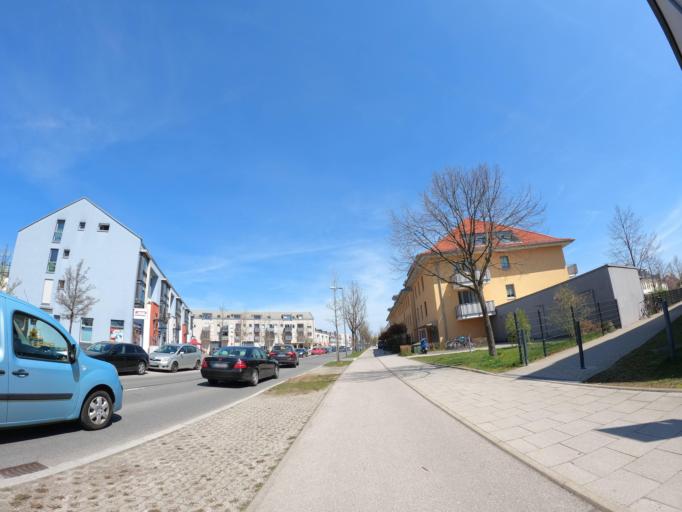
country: DE
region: Bavaria
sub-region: Upper Bavaria
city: Neubiberg
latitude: 48.1177
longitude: 11.6579
